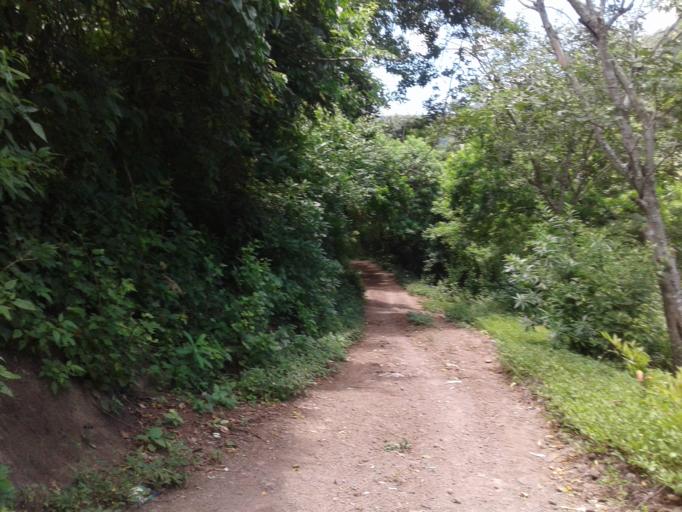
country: NI
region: Matagalpa
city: Terrabona
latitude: 12.8308
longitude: -85.9860
